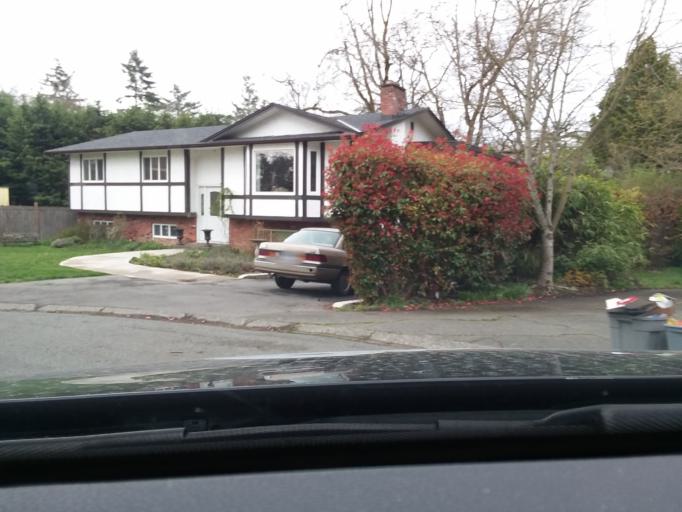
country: CA
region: British Columbia
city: Oak Bay
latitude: 48.4698
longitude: -123.3410
